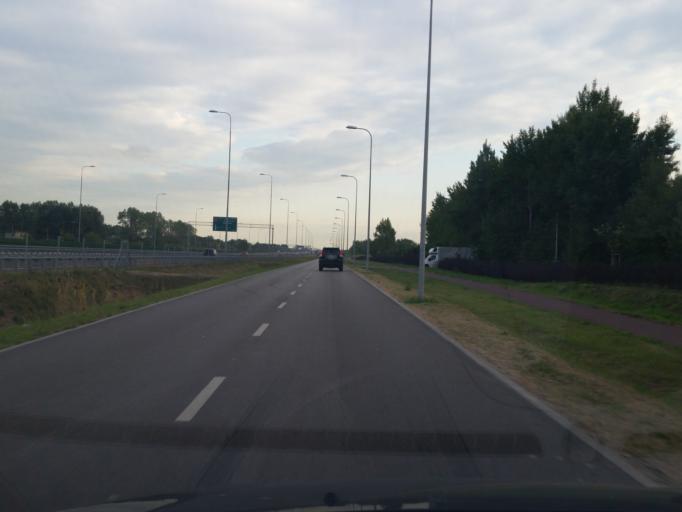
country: PL
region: Masovian Voivodeship
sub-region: Warszawa
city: Wlochy
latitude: 52.1531
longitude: 20.9872
